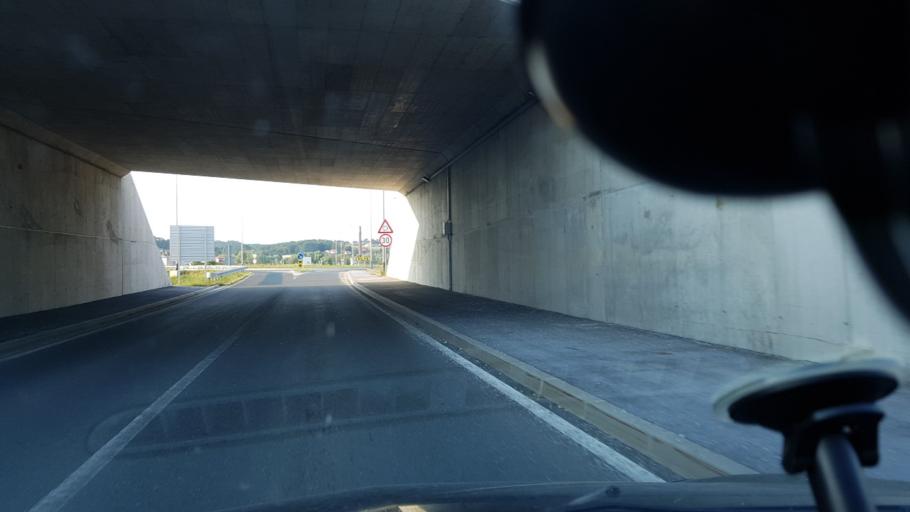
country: HR
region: Krapinsko-Zagorska
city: Bedekovcina
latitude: 46.0324
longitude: 15.9940
